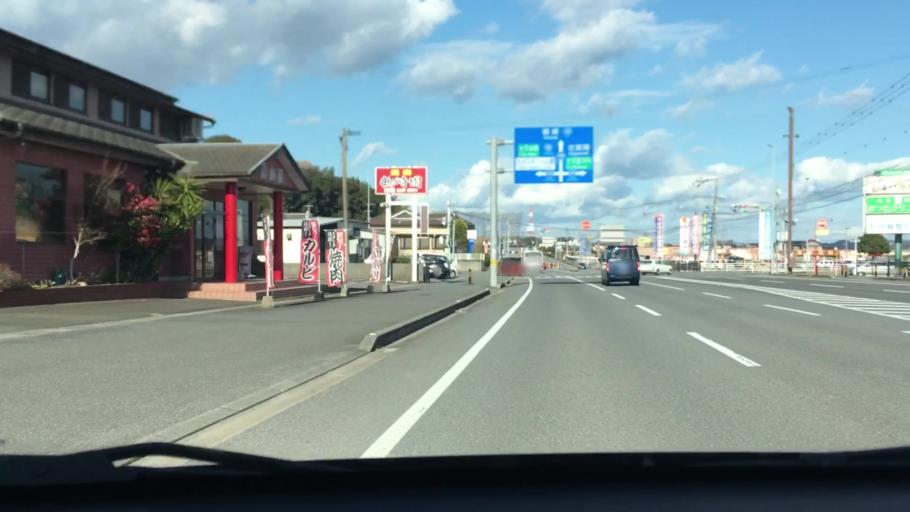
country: JP
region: Oita
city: Tsurusaki
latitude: 33.1895
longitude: 131.6712
